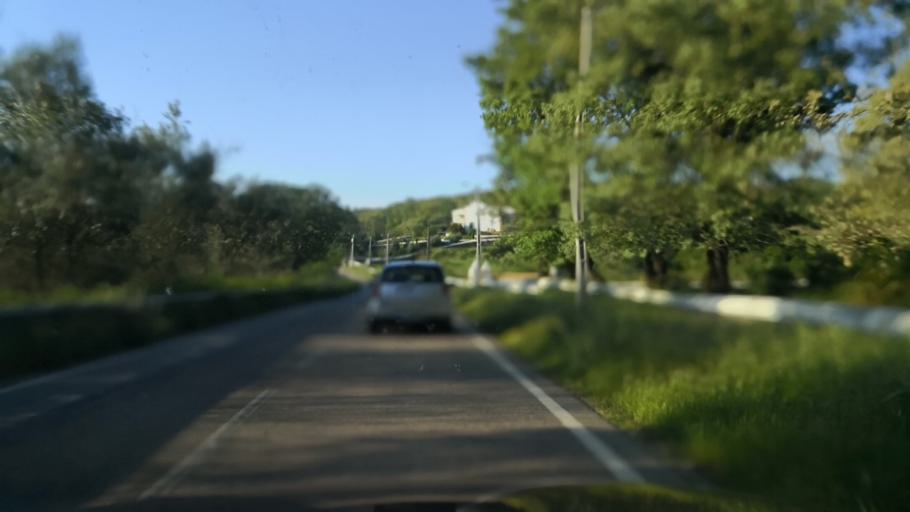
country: PT
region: Portalegre
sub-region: Marvao
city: Marvao
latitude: 39.3496
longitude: -7.4058
